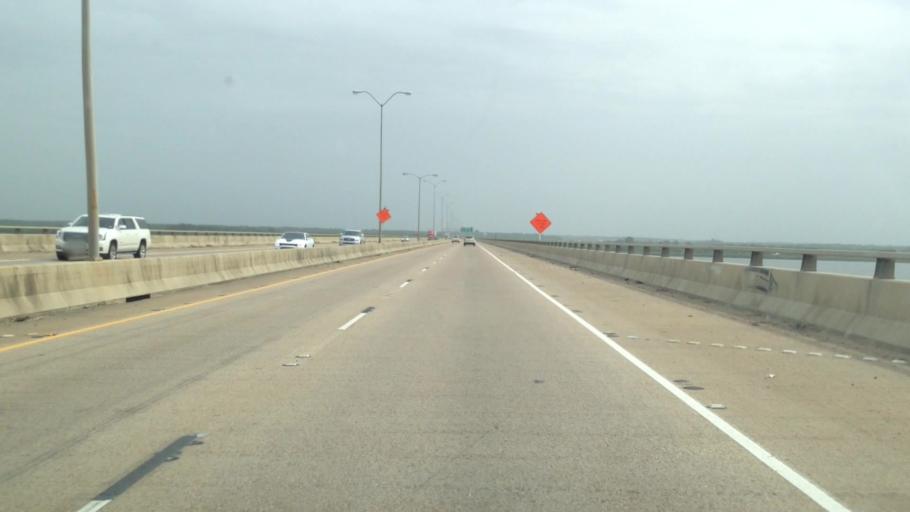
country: US
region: Louisiana
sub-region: Caddo Parish
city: Shreveport
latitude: 32.5084
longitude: -93.8146
